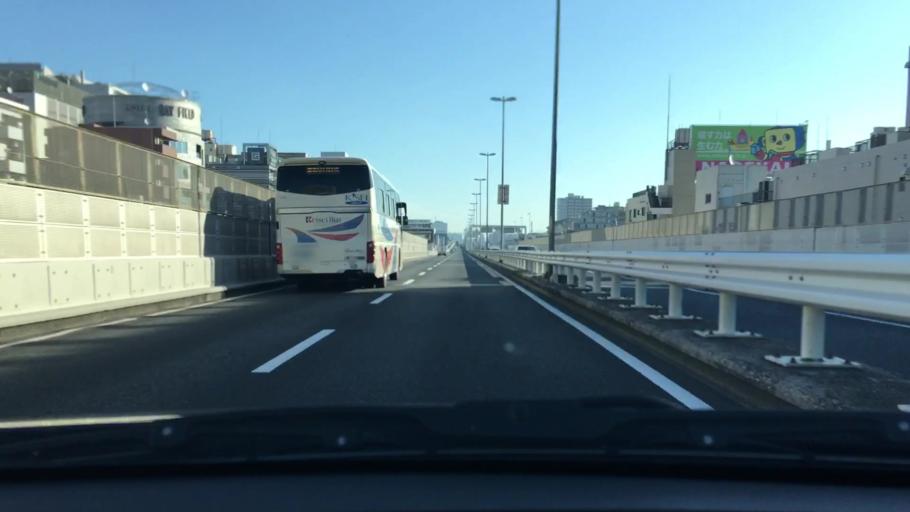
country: JP
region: Tokyo
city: Urayasu
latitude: 35.6932
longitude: 139.8159
